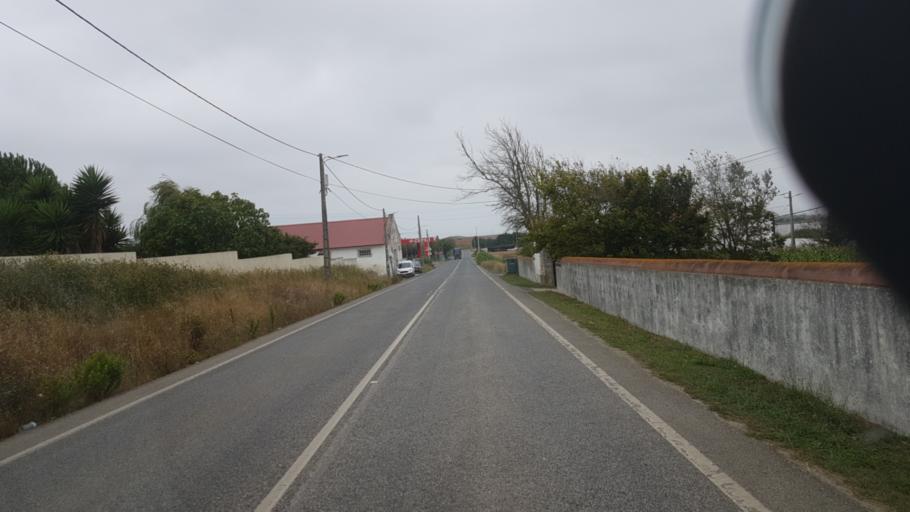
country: PT
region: Leiria
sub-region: Peniche
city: Atouguia da Baleia
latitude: 39.3302
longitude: -9.2757
